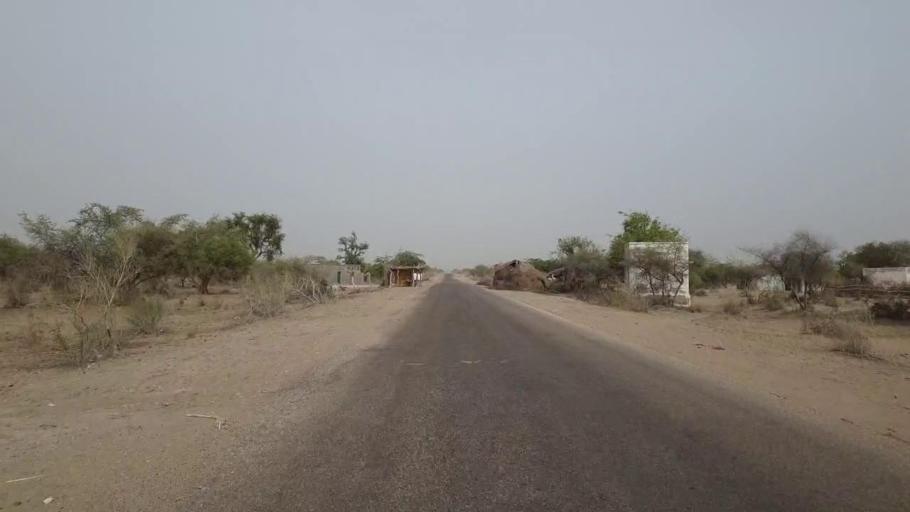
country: PK
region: Sindh
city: Islamkot
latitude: 24.5743
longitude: 70.3152
